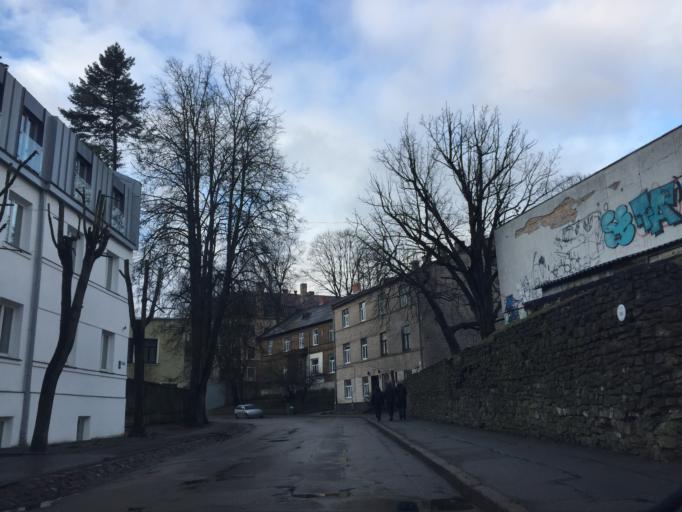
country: LV
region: Riga
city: Riga
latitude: 56.9371
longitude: 24.0755
